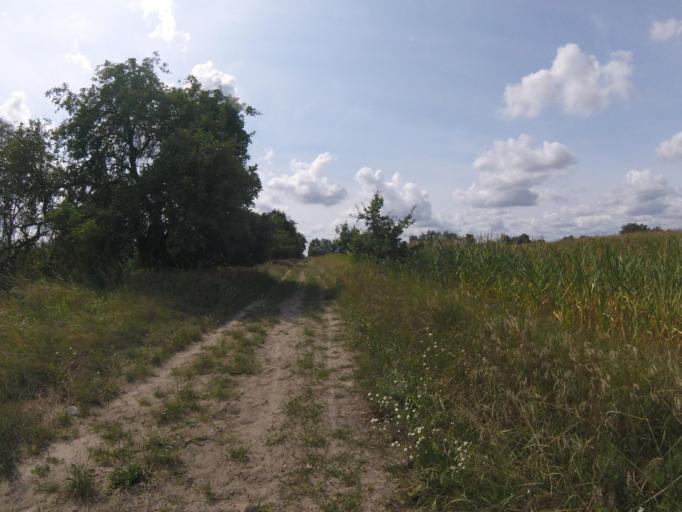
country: DE
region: Brandenburg
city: Mittenwalde
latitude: 52.2880
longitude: 13.5061
